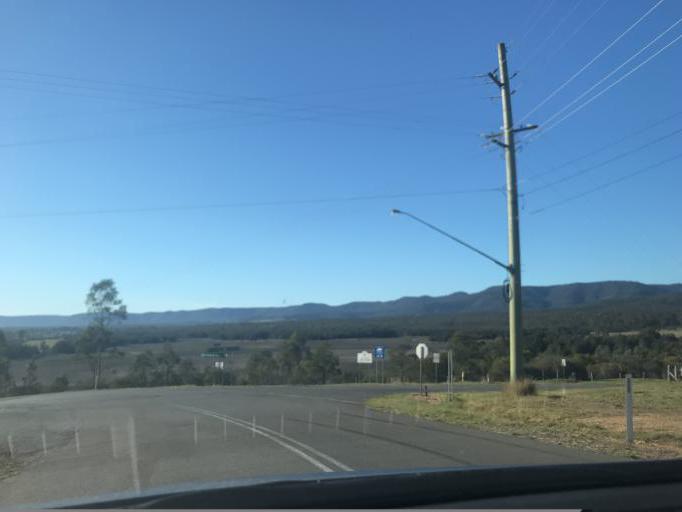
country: AU
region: New South Wales
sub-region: Cessnock
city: Cessnock
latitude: -32.9066
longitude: 151.2846
